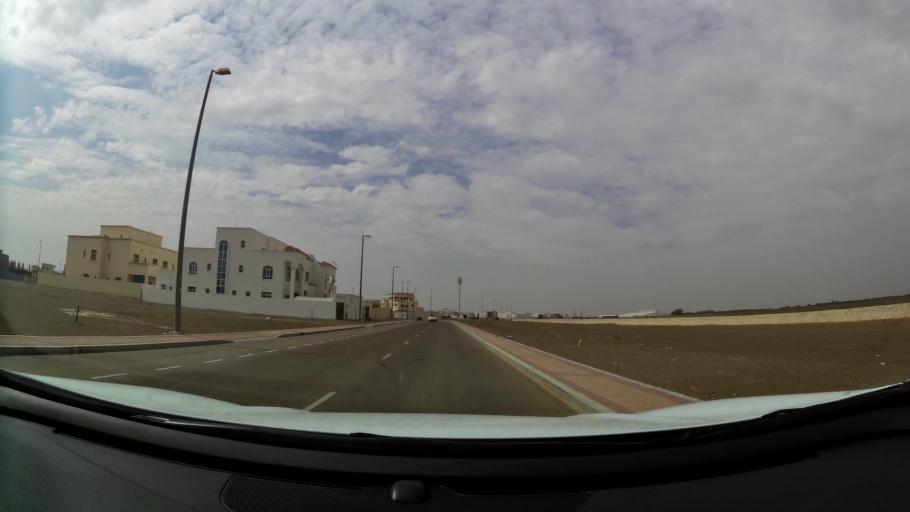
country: AE
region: Abu Dhabi
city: Al Ain
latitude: 24.1949
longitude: 55.8148
